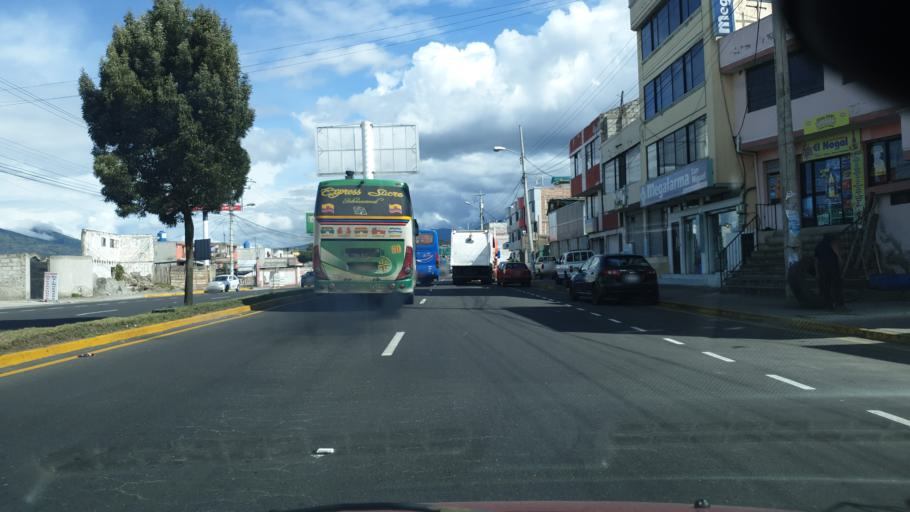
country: EC
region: Tungurahua
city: Ambato
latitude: -1.3045
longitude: -78.6371
